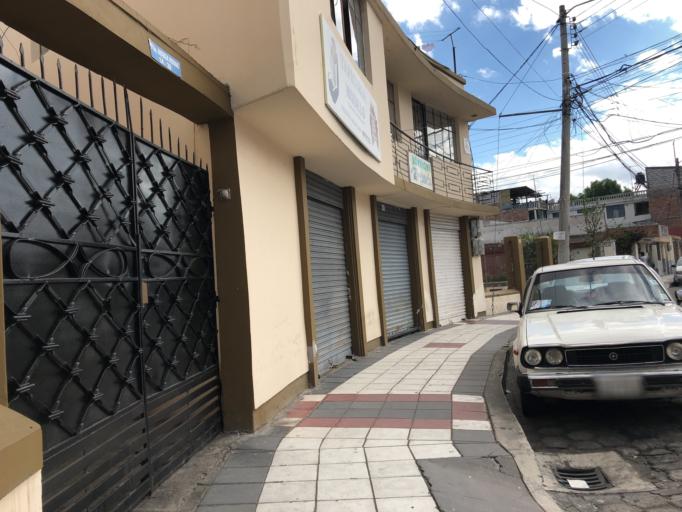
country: EC
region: Imbabura
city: Ibarra
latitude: 0.3506
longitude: -78.1239
